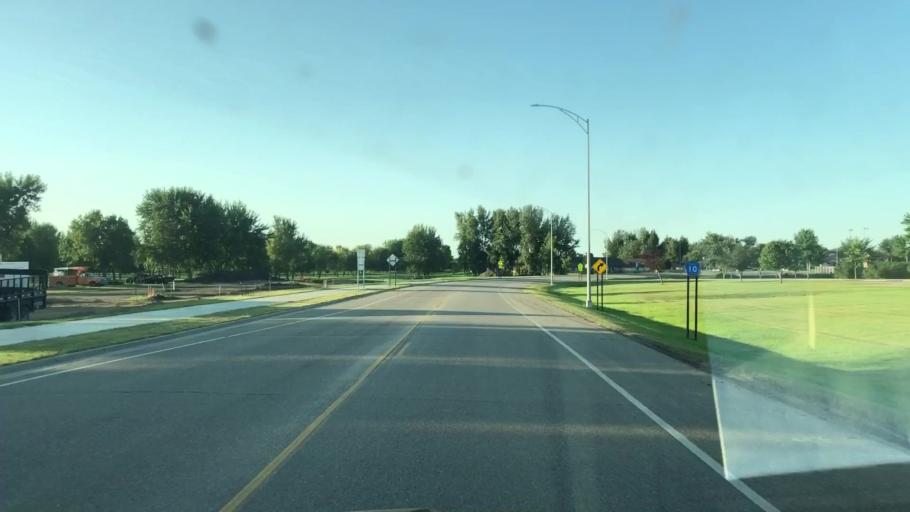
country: US
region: Minnesota
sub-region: Nobles County
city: Worthington
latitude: 43.6297
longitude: -95.6287
